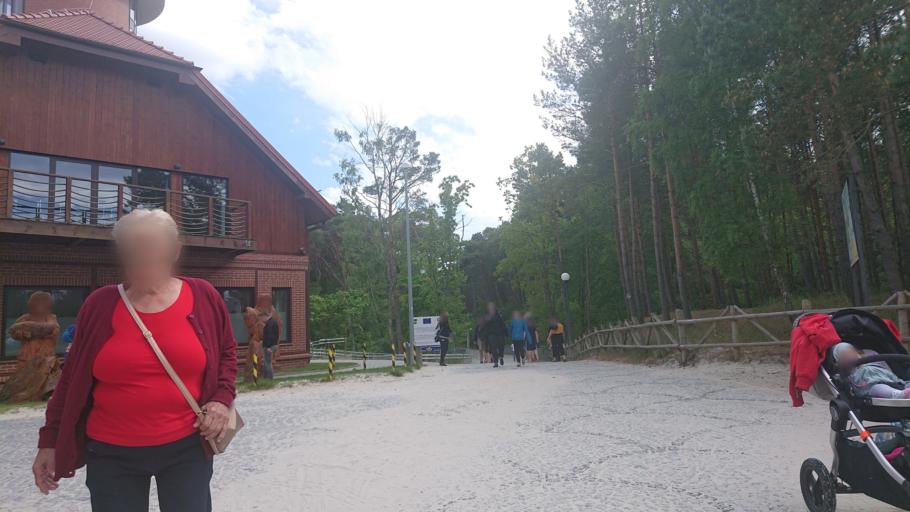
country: PL
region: Pomeranian Voivodeship
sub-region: Powiat pucki
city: Krokowa
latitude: 54.8326
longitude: 18.0881
